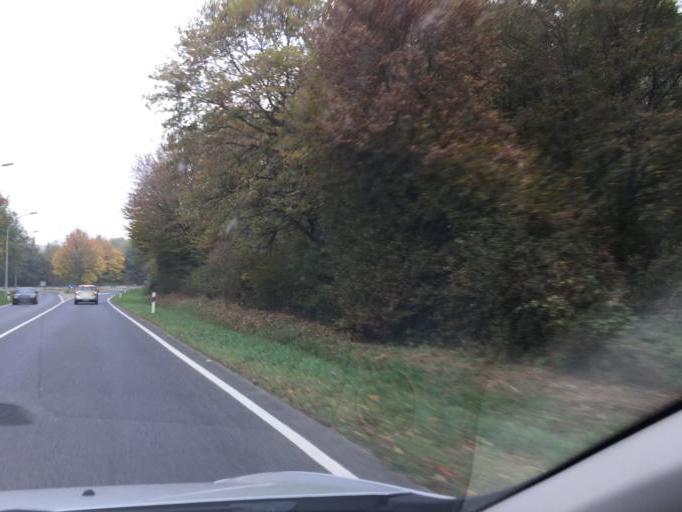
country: LU
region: Luxembourg
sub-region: Canton de Luxembourg
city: Sandweiler
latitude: 49.6075
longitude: 6.2304
